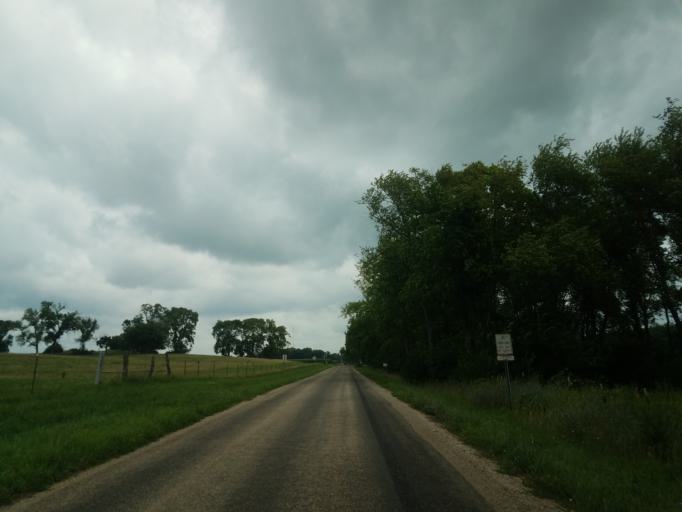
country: US
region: Illinois
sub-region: McLean County
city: Twin Grove
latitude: 40.4595
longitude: -89.0449
